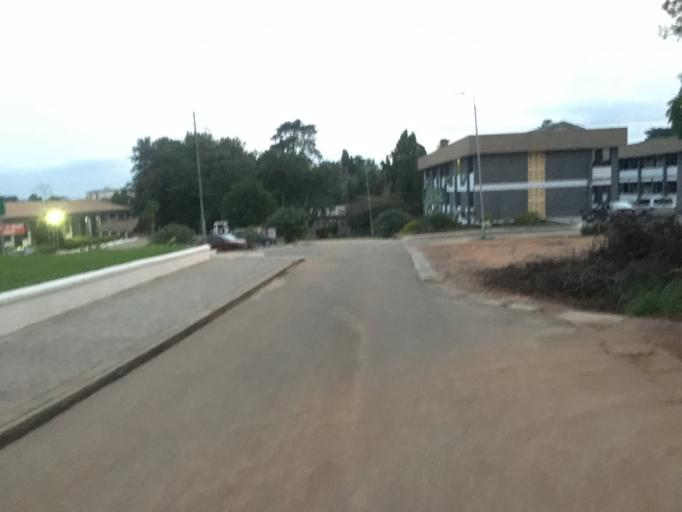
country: GH
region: Ashanti
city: Kumasi
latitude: 6.6732
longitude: -1.5682
